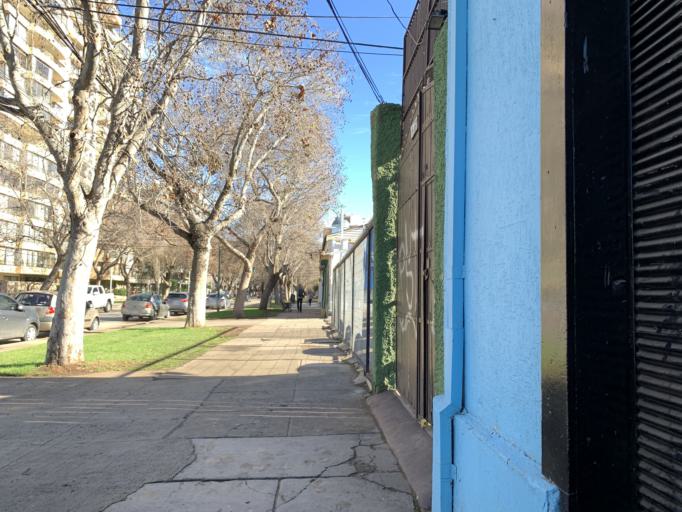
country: CL
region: Valparaiso
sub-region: Provincia de Valparaiso
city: Vina del Mar
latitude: -33.0160
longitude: -71.5452
